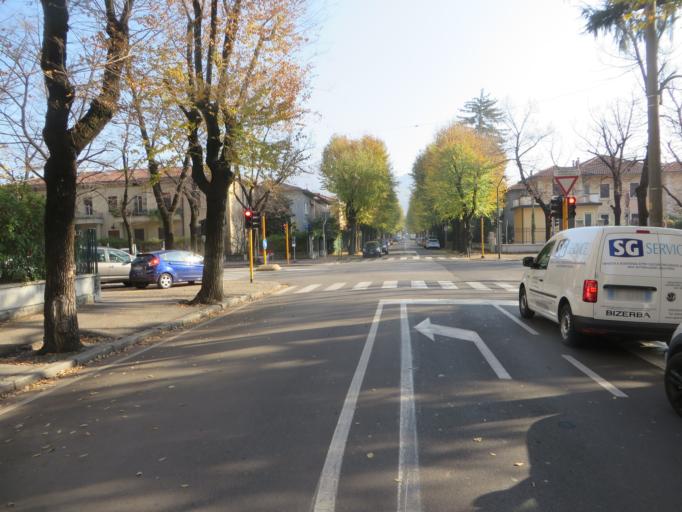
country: IT
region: Lombardy
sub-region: Provincia di Brescia
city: Brescia
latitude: 45.5510
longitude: 10.2150
